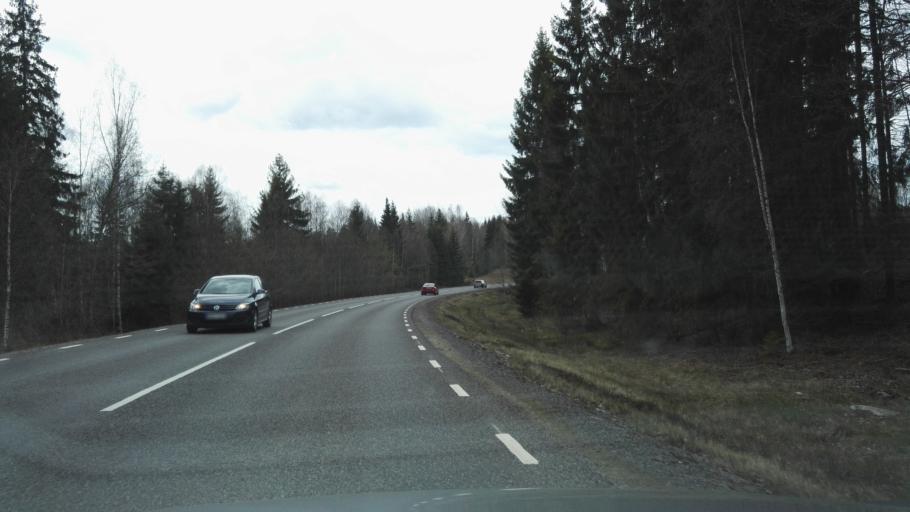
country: SE
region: Kronoberg
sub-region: Vaxjo Kommun
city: Braas
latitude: 57.0543
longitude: 15.0452
